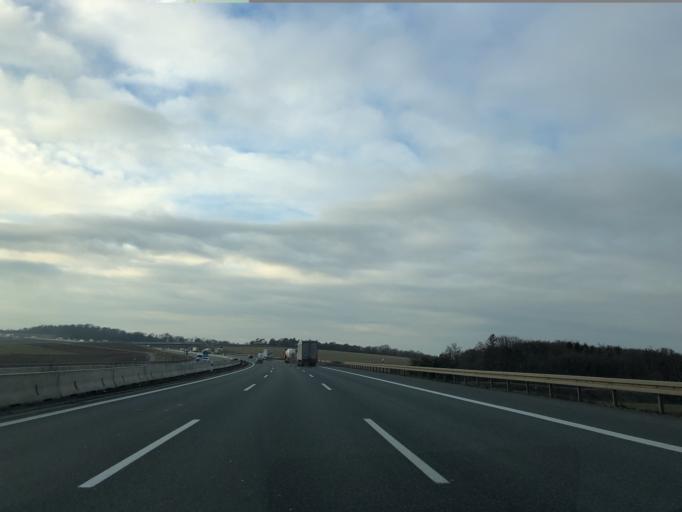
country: DE
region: Bavaria
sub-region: Regierungsbezirk Unterfranken
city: Uettingen
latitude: 49.7745
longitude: 9.7375
